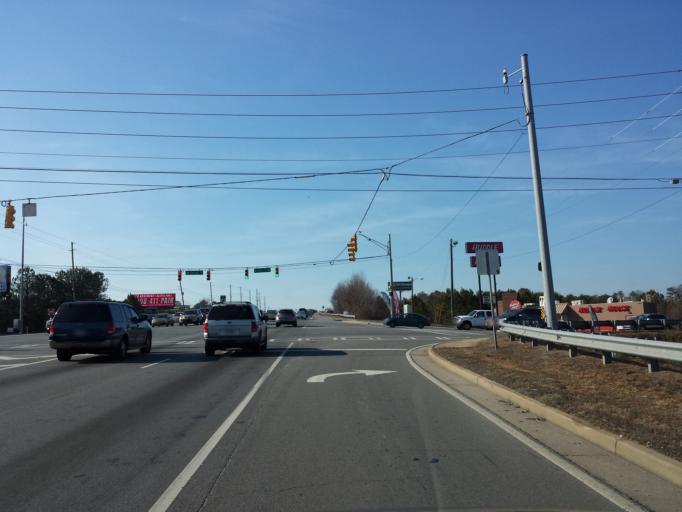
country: US
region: Georgia
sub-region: Cobb County
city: Kennesaw
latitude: 34.0111
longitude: -84.6102
